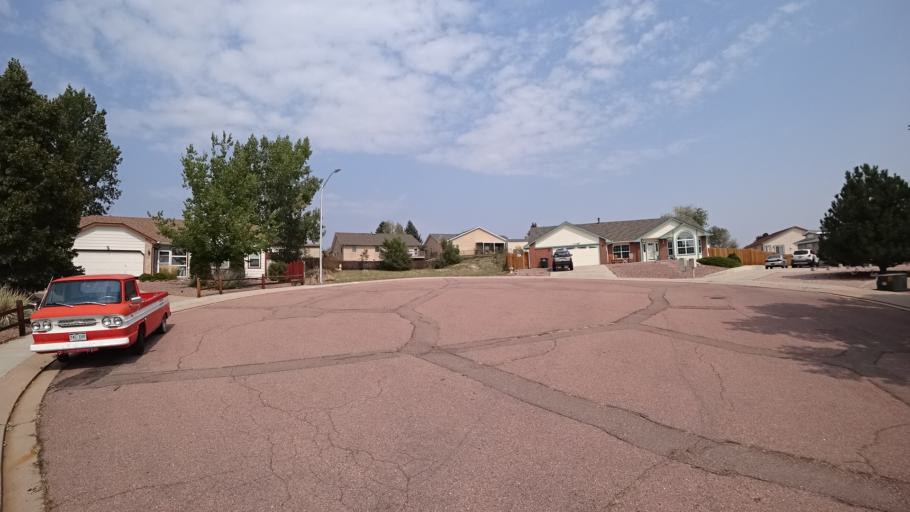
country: US
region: Colorado
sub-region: El Paso County
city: Stratmoor
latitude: 38.8238
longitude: -104.7660
